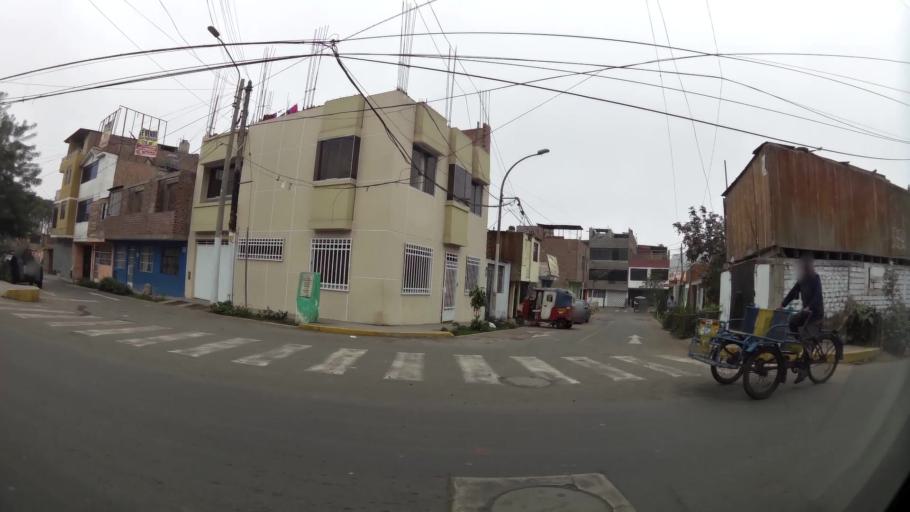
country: PE
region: Lima
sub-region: Lima
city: Carabayllo
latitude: -11.8702
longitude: -77.0758
